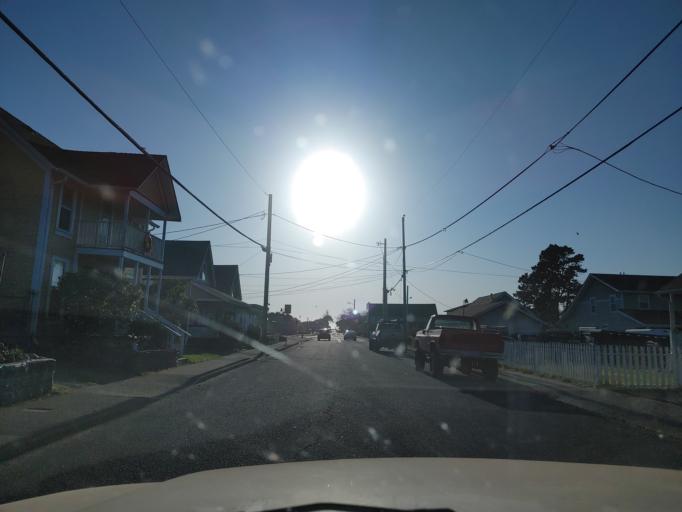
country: US
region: Oregon
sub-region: Clatsop County
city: Seaside
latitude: 46.0015
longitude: -123.9195
